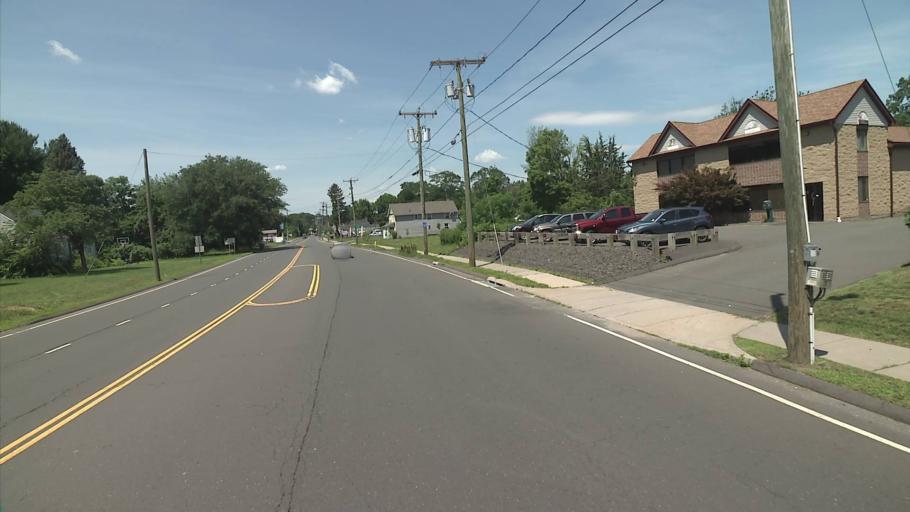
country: US
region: Connecticut
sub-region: Hartford County
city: Plainville
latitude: 41.6731
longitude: -72.8875
